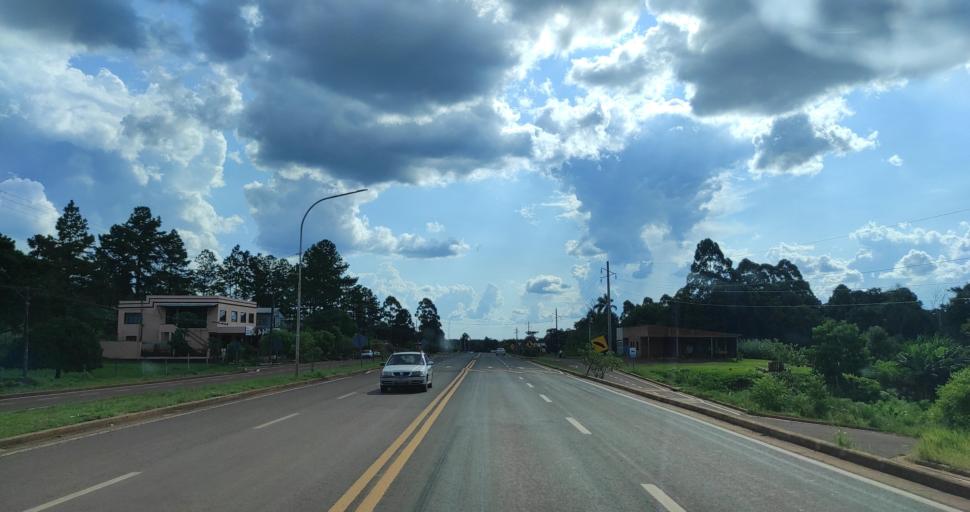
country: AR
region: Misiones
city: Bernardo de Irigoyen
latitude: -26.2939
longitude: -53.7443
